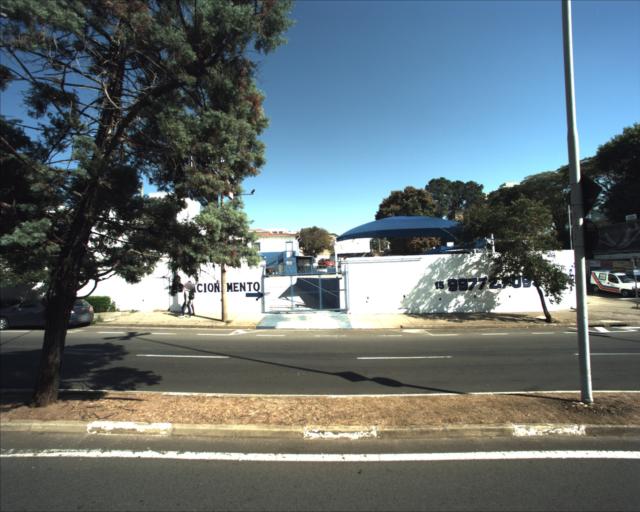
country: BR
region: Sao Paulo
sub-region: Sorocaba
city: Sorocaba
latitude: -23.5086
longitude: -47.4557
